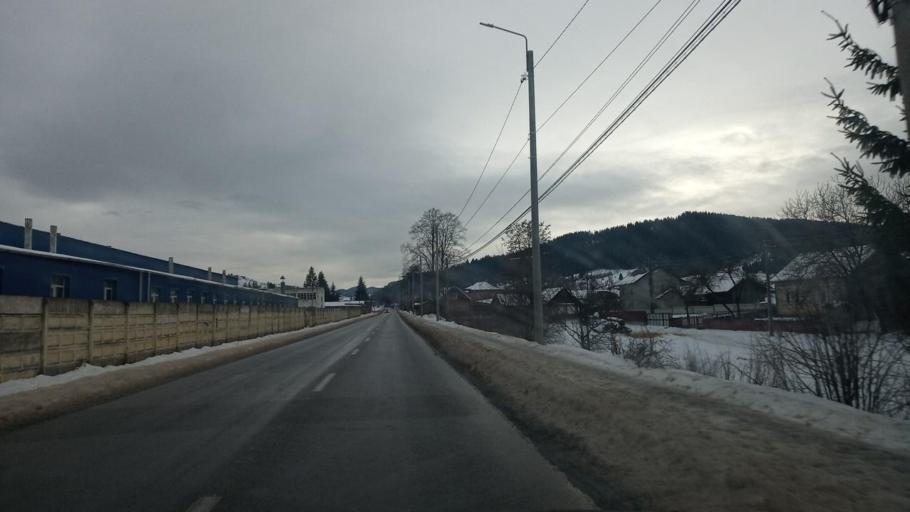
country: RO
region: Suceava
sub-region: Comuna Frasin
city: Frasin
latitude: 47.5325
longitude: 25.7984
